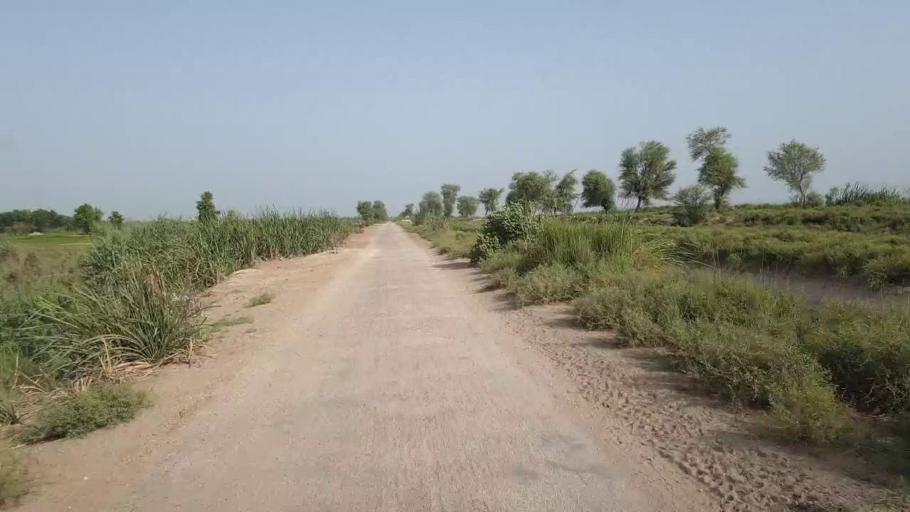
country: PK
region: Sindh
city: Daur
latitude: 26.3382
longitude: 68.1841
